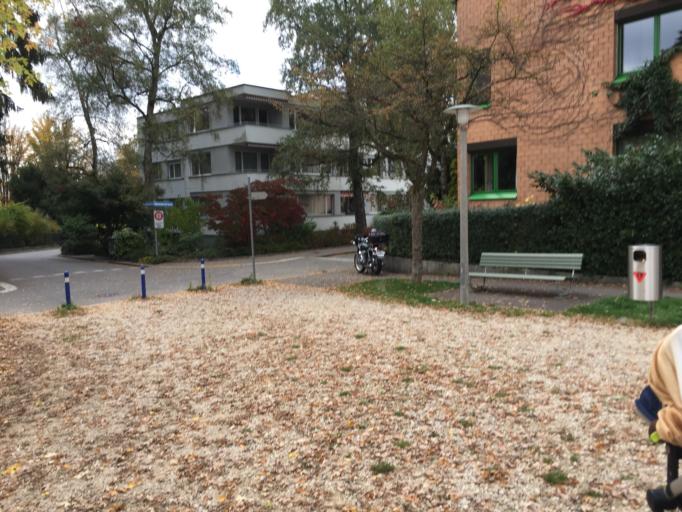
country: CH
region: Zurich
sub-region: Bezirk Zuerich
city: Zuerich (Kreis 11) / Oerlikon
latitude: 47.4049
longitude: 8.5426
